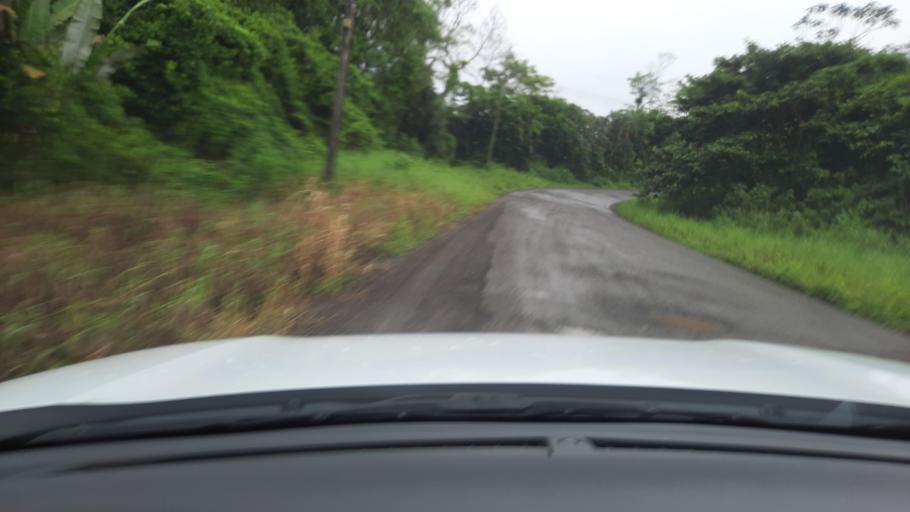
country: CR
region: Alajuela
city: San Jose
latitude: 11.0136
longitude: -85.3277
